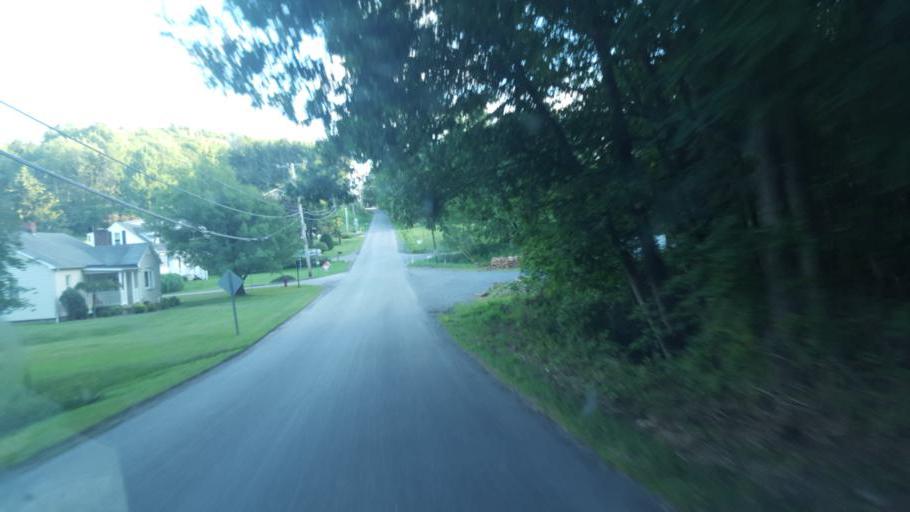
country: US
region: Pennsylvania
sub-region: Clarion County
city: Knox
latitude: 41.2290
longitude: -79.5387
